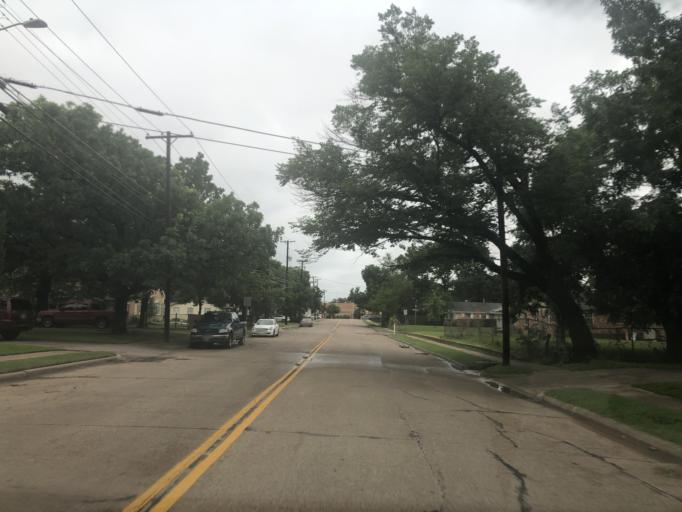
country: US
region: Texas
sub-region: Dallas County
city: Irving
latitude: 32.7960
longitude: -96.9469
